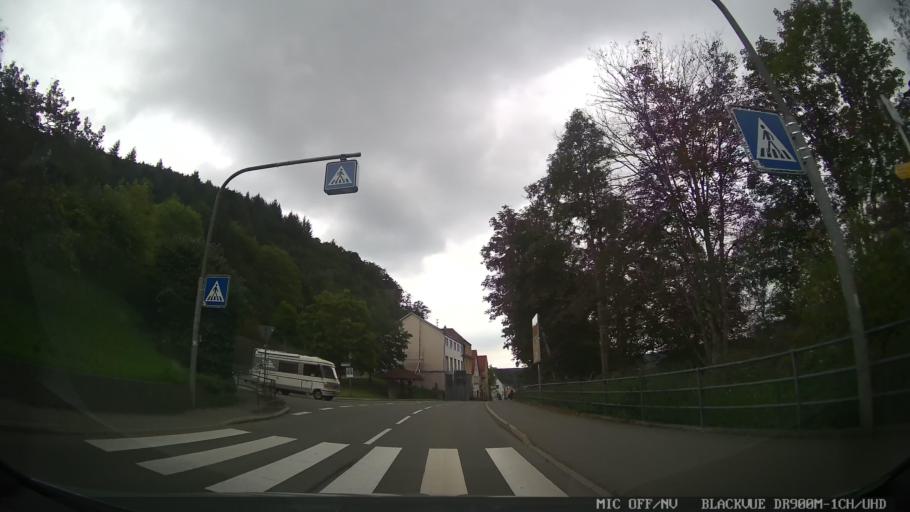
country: DE
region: Baden-Wuerttemberg
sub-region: Freiburg Region
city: Fridingen an der Donau
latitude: 48.0273
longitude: 8.9355
